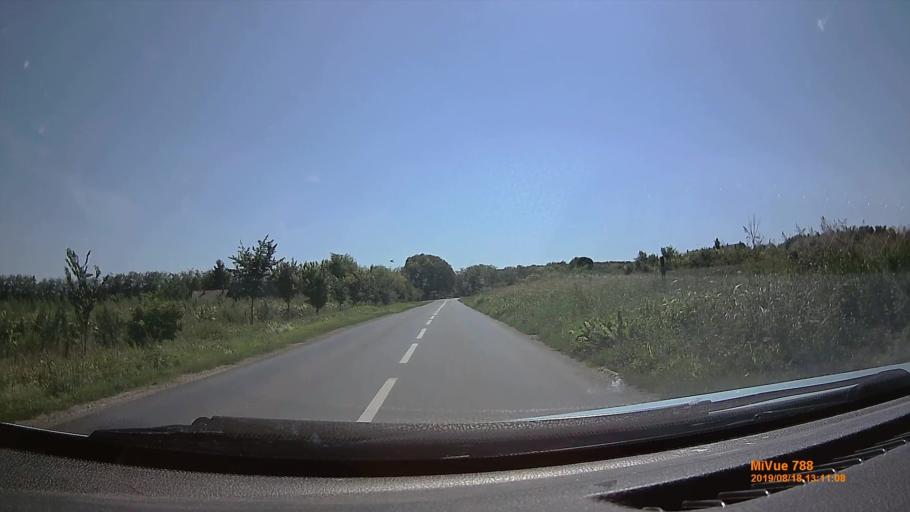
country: HU
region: Fejer
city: Kaloz
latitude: 46.9064
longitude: 18.5189
